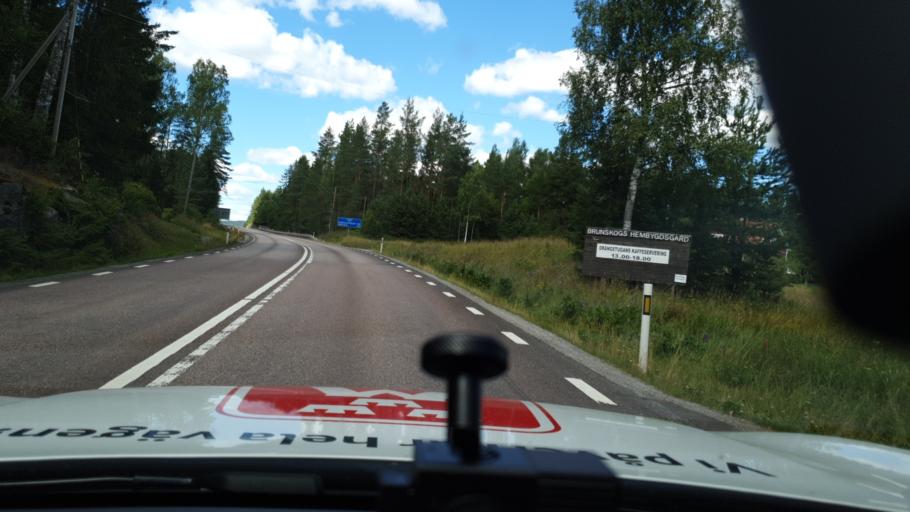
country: SE
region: Vaermland
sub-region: Sunne Kommun
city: Sunne
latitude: 59.6565
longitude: 12.9422
